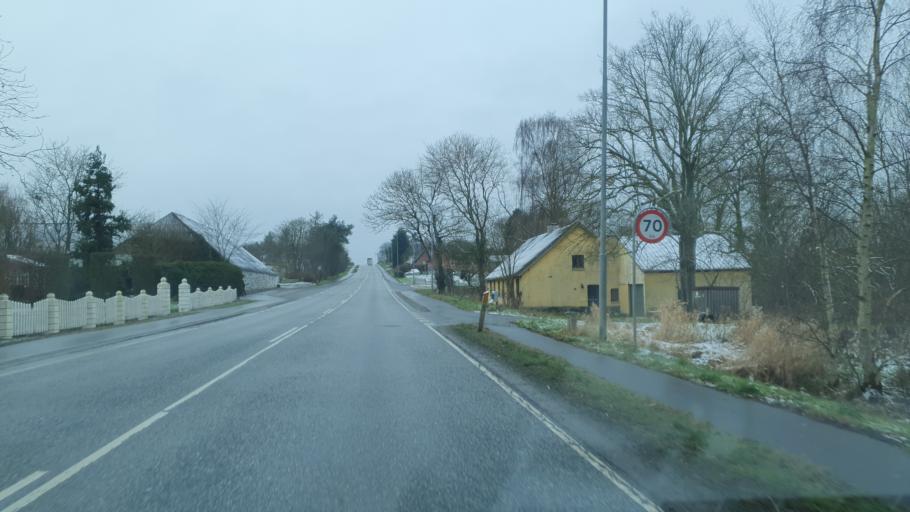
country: DK
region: North Denmark
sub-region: Jammerbugt Kommune
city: Brovst
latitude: 57.0950
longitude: 9.4785
